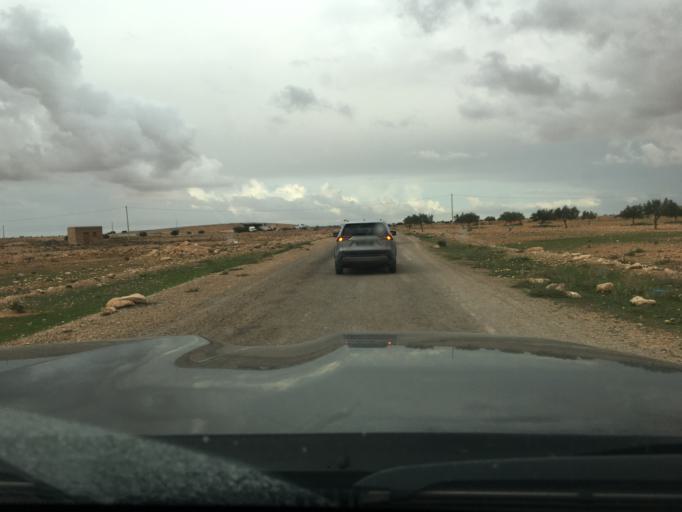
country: TN
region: Madanin
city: Medenine
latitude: 33.2945
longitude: 10.6089
